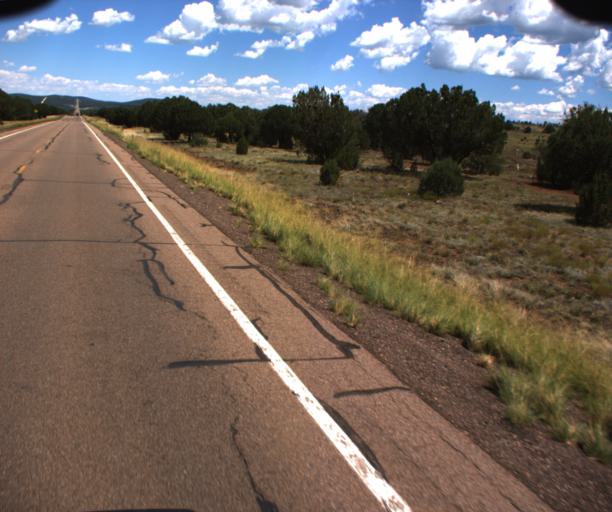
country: US
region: Arizona
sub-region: Navajo County
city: White Mountain Lake
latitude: 34.2767
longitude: -109.8897
